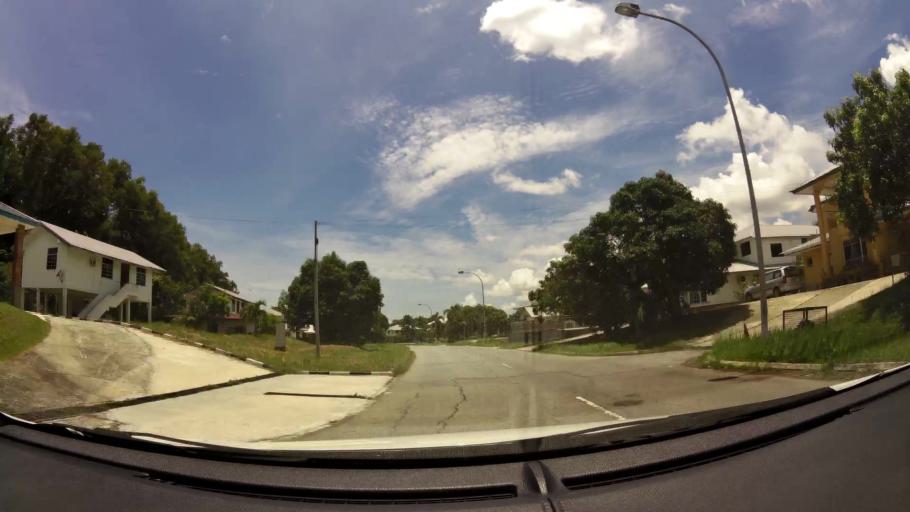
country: BN
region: Brunei and Muara
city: Bandar Seri Begawan
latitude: 4.9605
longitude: 114.9218
